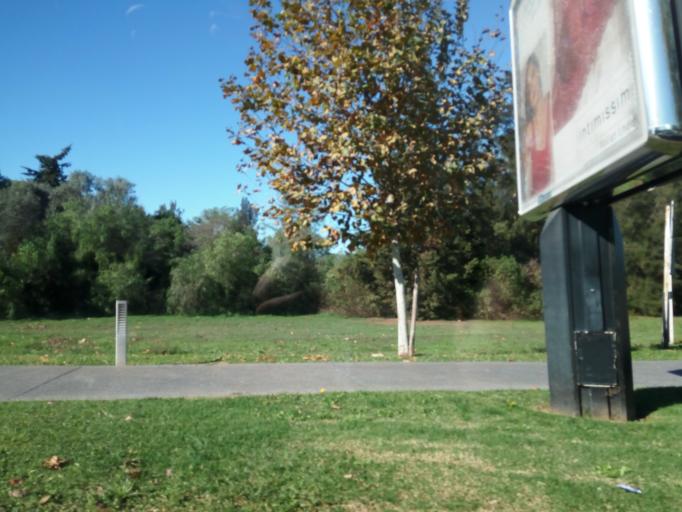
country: PT
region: Faro
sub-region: Loule
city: Vilamoura
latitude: 37.1024
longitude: -8.1246
